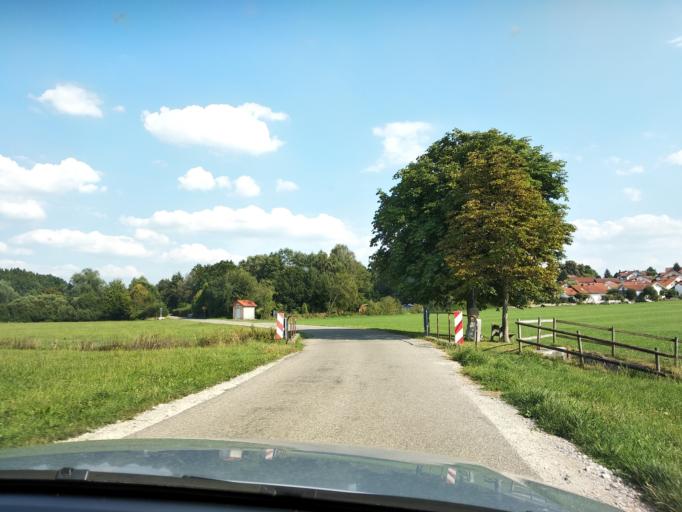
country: DE
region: Bavaria
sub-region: Swabia
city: Trunkelsberg
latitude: 48.0040
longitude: 10.2059
